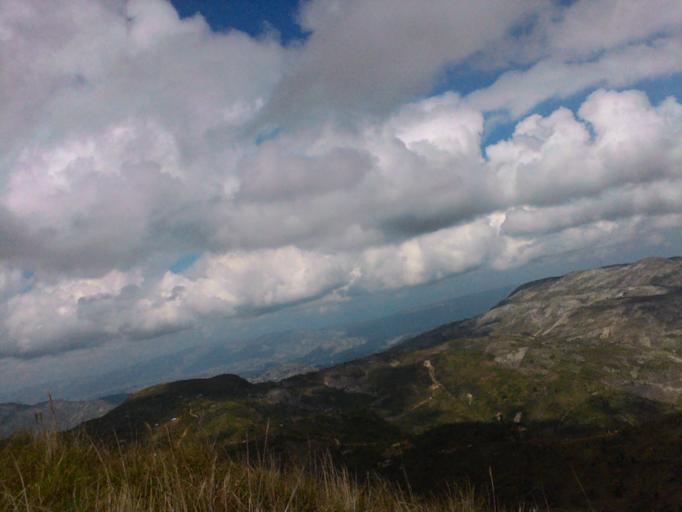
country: HT
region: Sud
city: Les Anglais
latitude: 18.4484
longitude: -74.1055
